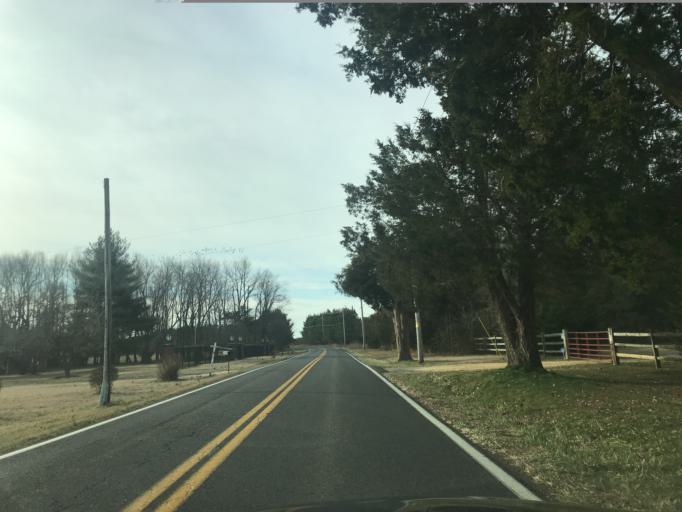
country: US
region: Maryland
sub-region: Charles County
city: Hughesville
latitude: 38.5280
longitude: -76.8423
